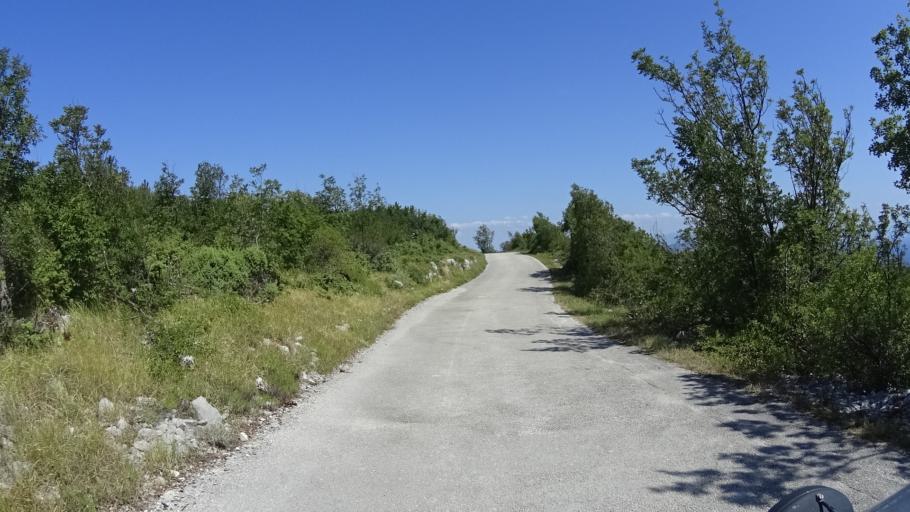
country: HR
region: Istarska
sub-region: Grad Labin
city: Rabac
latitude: 44.9876
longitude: 14.1458
